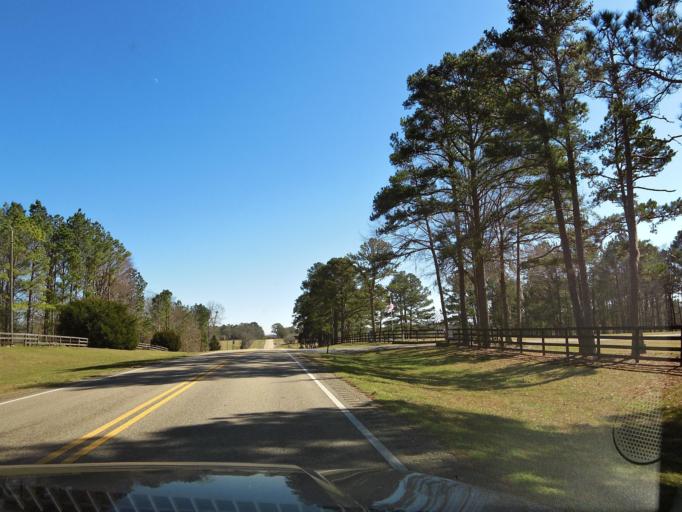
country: US
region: Alabama
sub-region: Montgomery County
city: Pike Road
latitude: 32.1843
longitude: -86.0954
